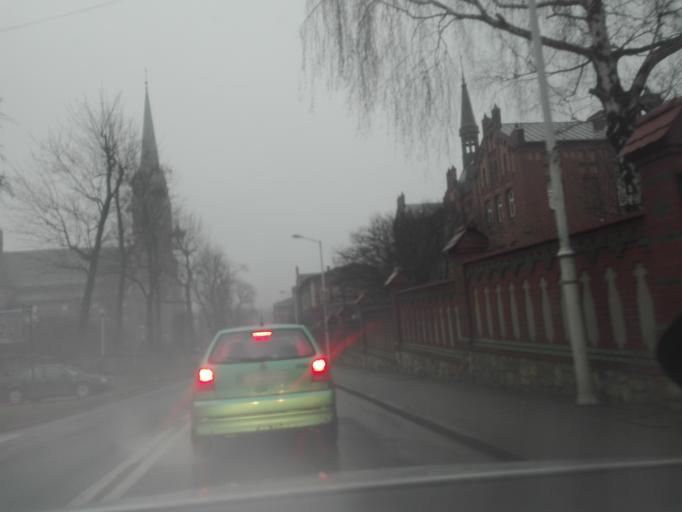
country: PL
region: Silesian Voivodeship
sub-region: Katowice
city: Katowice
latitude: 50.2701
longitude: 19.0402
